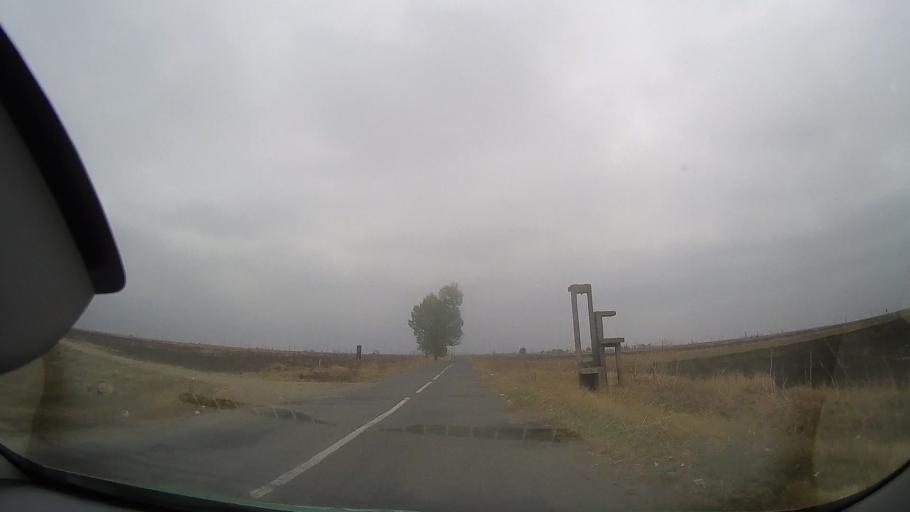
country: RO
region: Buzau
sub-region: Comuna Glodeanu-Silistea
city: Glodeanu-Silistea
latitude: 44.8101
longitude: 26.8561
